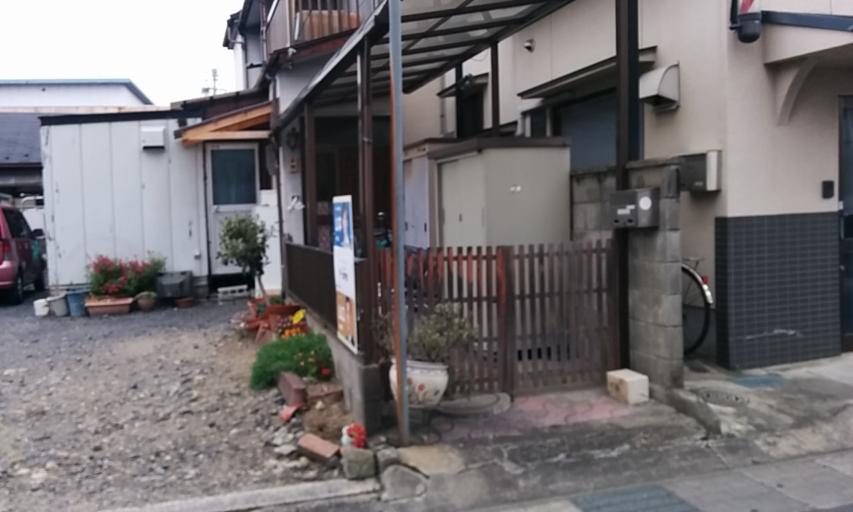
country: JP
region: Shiga Prefecture
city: Kusatsu
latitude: 35.0080
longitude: 135.9541
